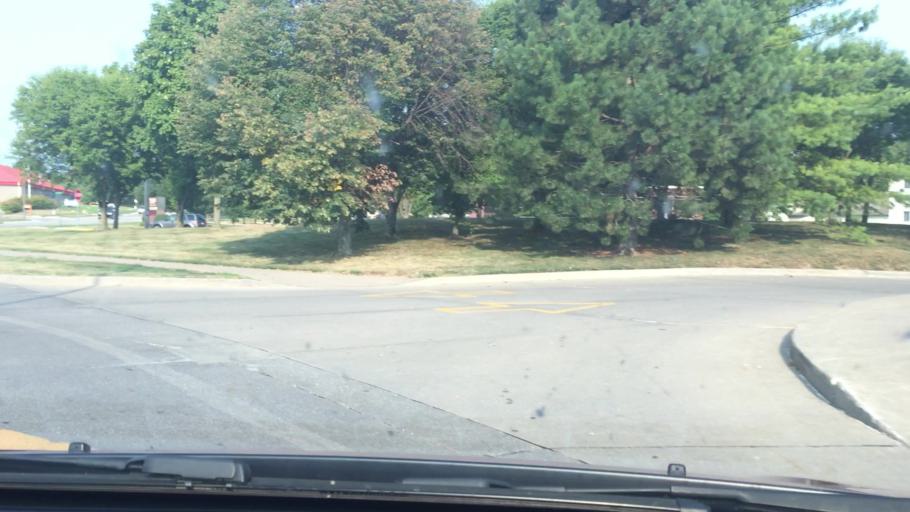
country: US
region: Iowa
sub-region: Muscatine County
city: Muscatine
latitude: 41.4510
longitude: -91.0360
